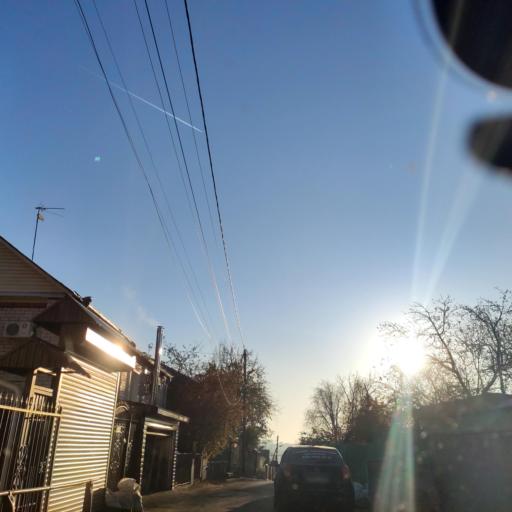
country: RU
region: Voronezj
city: Voronezh
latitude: 51.7086
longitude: 39.2324
